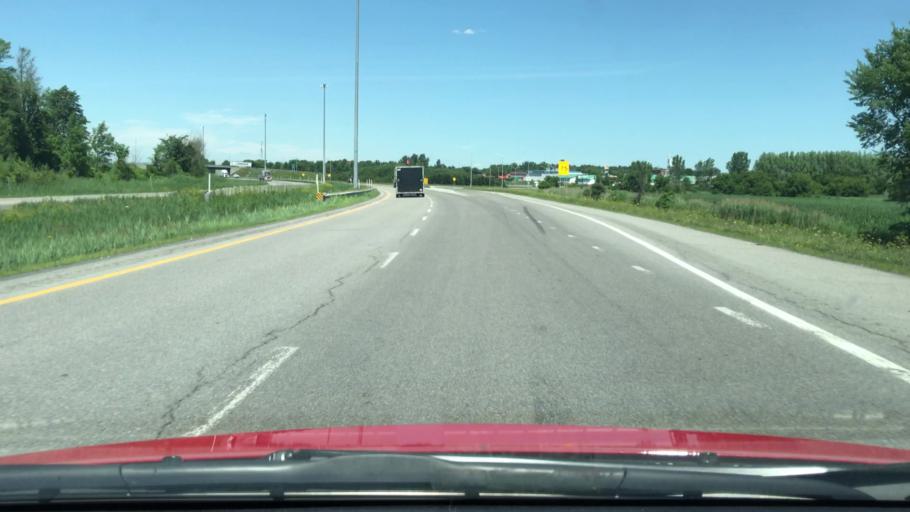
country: CA
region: Quebec
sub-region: Monteregie
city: Napierville
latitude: 45.1879
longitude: -73.4534
